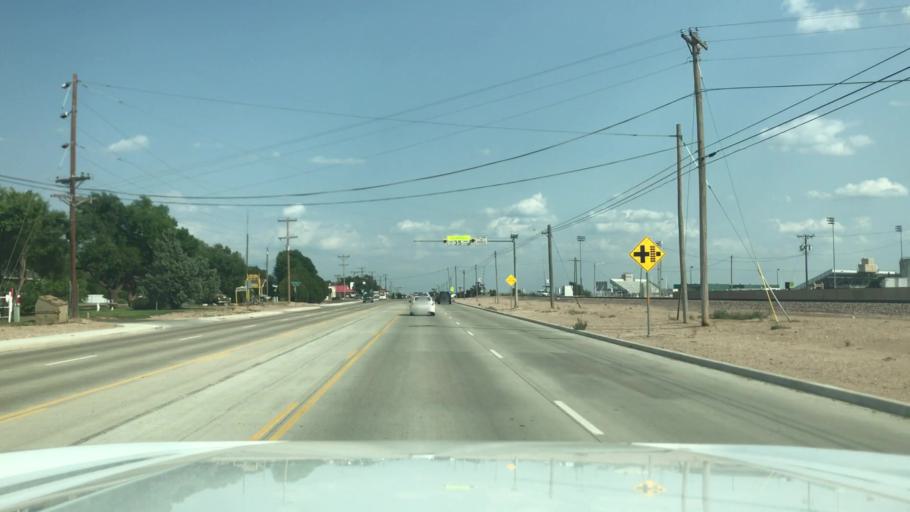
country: US
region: Texas
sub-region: Dallam County
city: Dalhart
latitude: 36.0524
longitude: -102.5029
